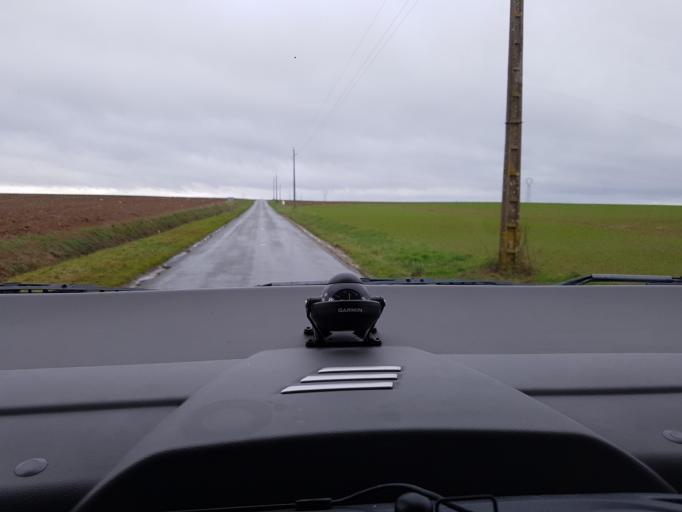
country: FR
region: Haute-Normandie
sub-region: Departement de l'Eure
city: Pont-Saint-Pierre
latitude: 49.3025
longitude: 1.3253
